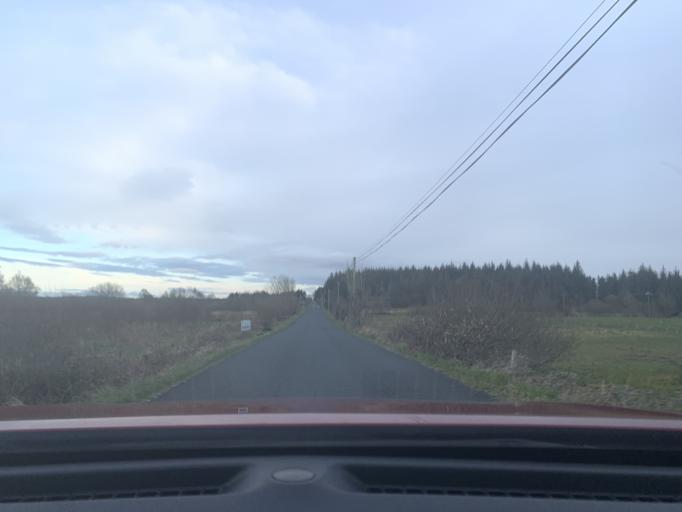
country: IE
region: Connaught
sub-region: Roscommon
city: Ballaghaderreen
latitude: 53.8870
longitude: -8.5692
